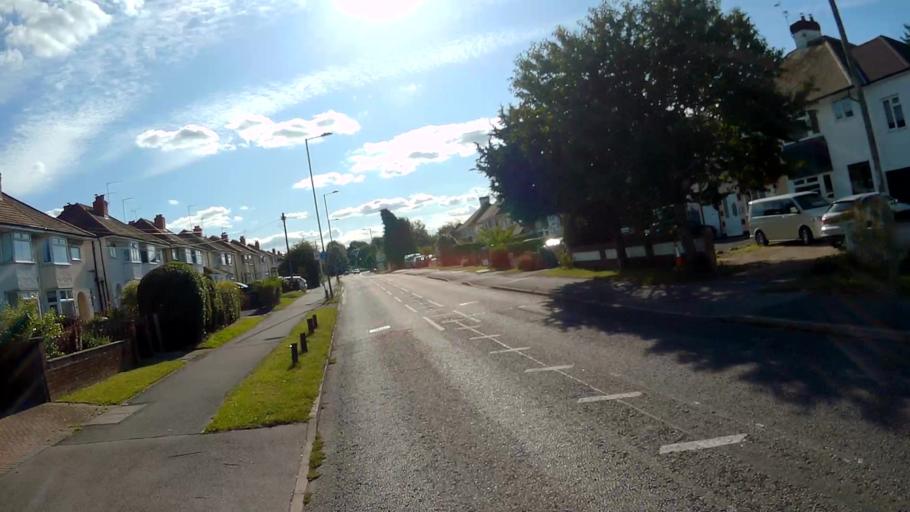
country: GB
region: England
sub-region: Hampshire
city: Basingstoke
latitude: 51.2568
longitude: -1.1005
